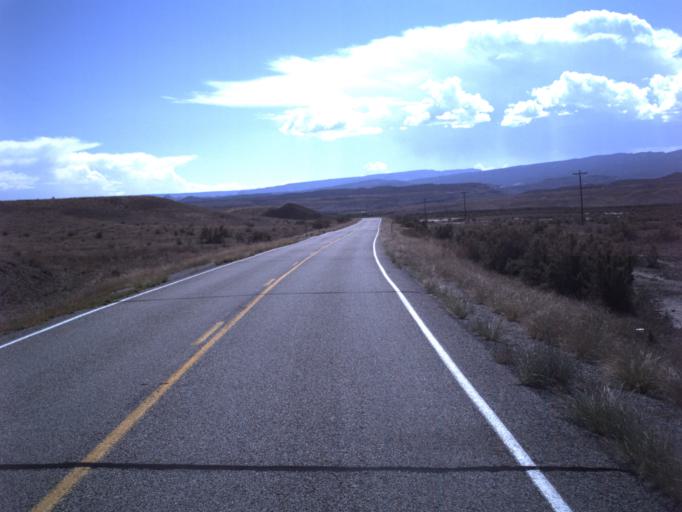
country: US
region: Utah
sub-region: Grand County
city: Moab
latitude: 38.8746
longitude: -109.3053
